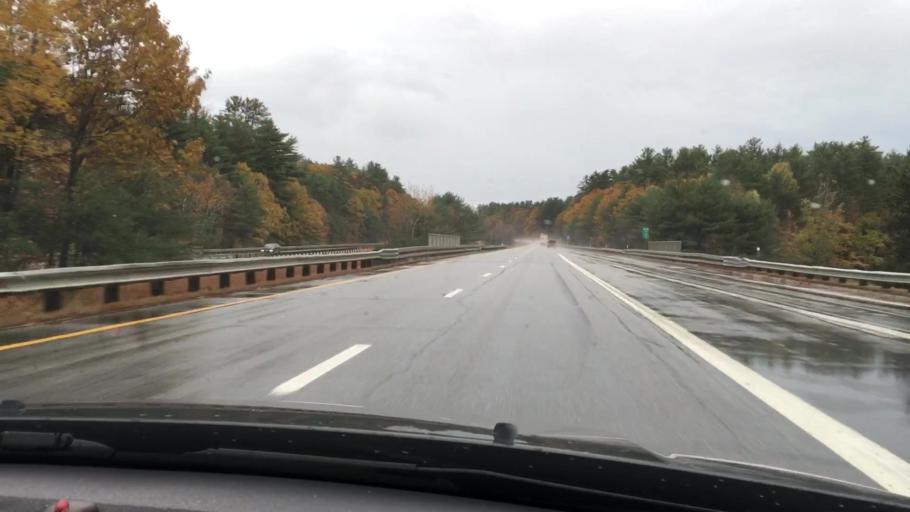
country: US
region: New Hampshire
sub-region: Grafton County
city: Ashland
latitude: 43.6139
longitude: -71.6429
